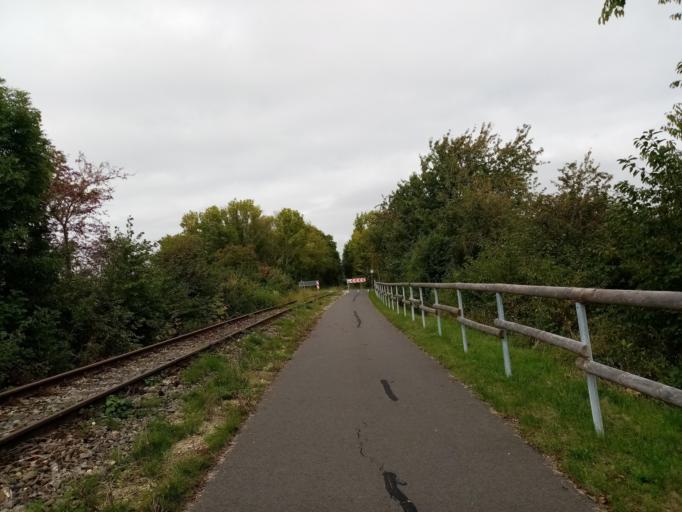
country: DE
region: Thuringia
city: Dingelstadt
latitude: 51.3034
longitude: 10.3053
